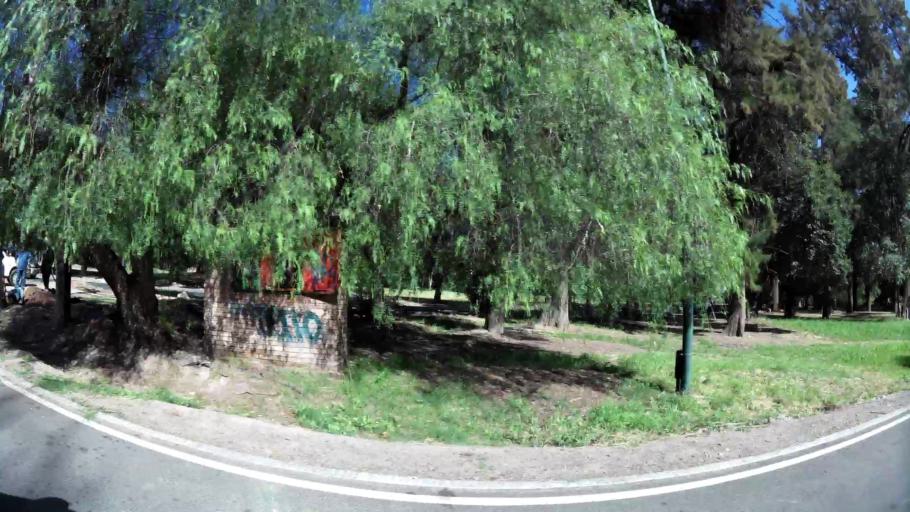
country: AR
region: Mendoza
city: Mendoza
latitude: -32.8912
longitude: -68.8733
